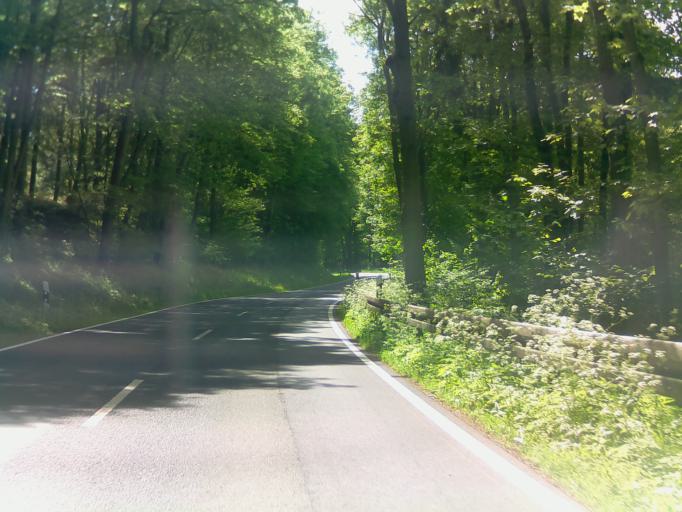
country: DE
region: Bavaria
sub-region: Regierungsbezirk Unterfranken
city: Arnstein
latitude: 49.9996
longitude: 9.9845
